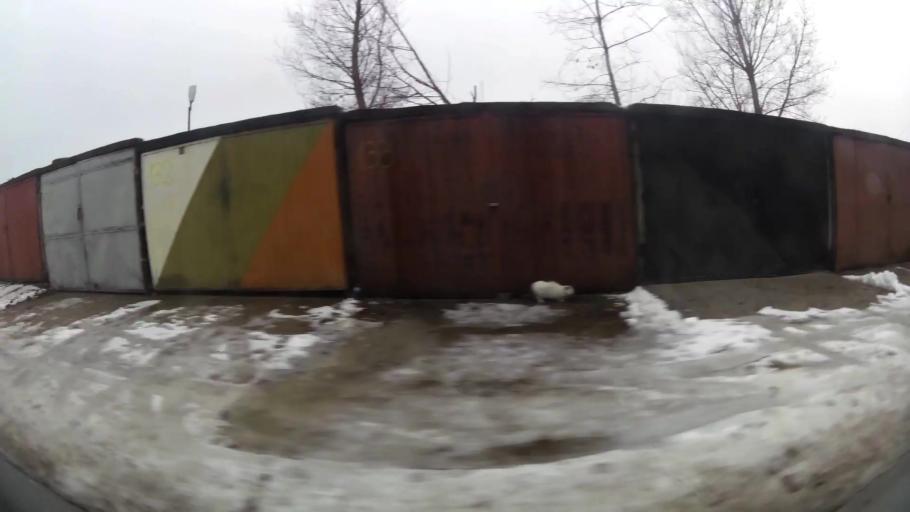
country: BG
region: Sofia-Capital
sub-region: Stolichna Obshtina
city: Sofia
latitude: 42.6863
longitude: 23.2604
